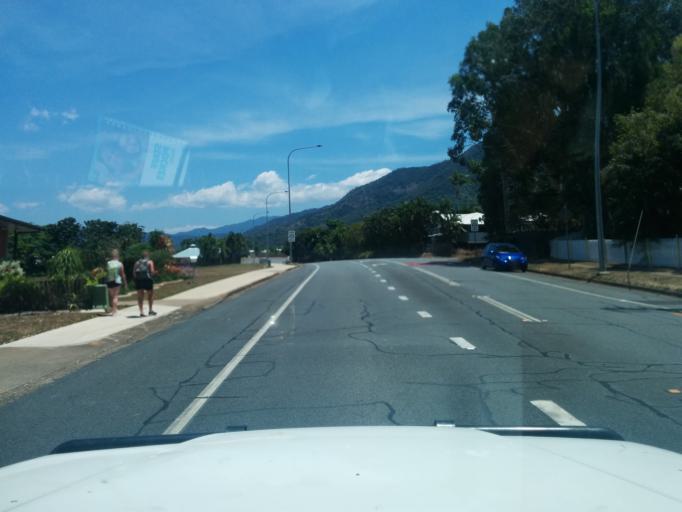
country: AU
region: Queensland
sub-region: Cairns
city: Redlynch
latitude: -16.8893
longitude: 145.6963
